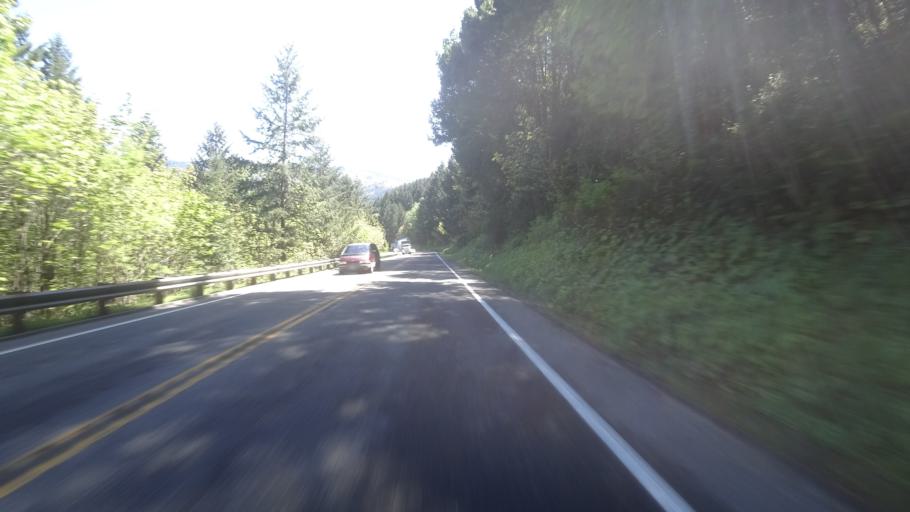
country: US
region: California
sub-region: Humboldt County
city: Blue Lake
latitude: 40.9053
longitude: -123.8206
